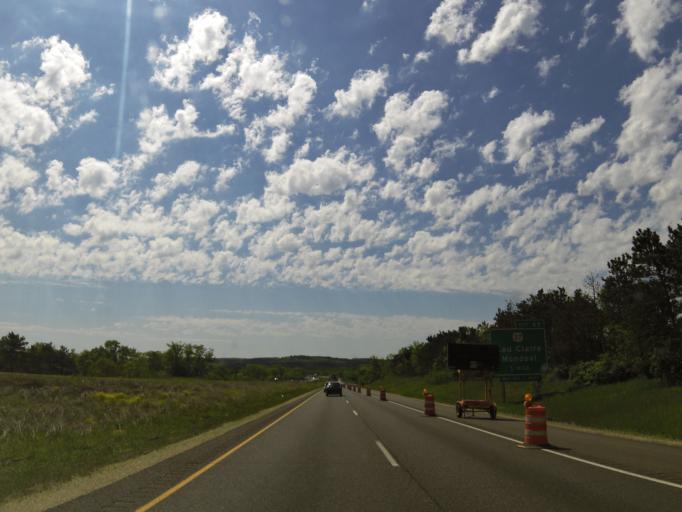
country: US
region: Wisconsin
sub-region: Eau Claire County
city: Eau Claire
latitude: 44.7903
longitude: -91.5477
